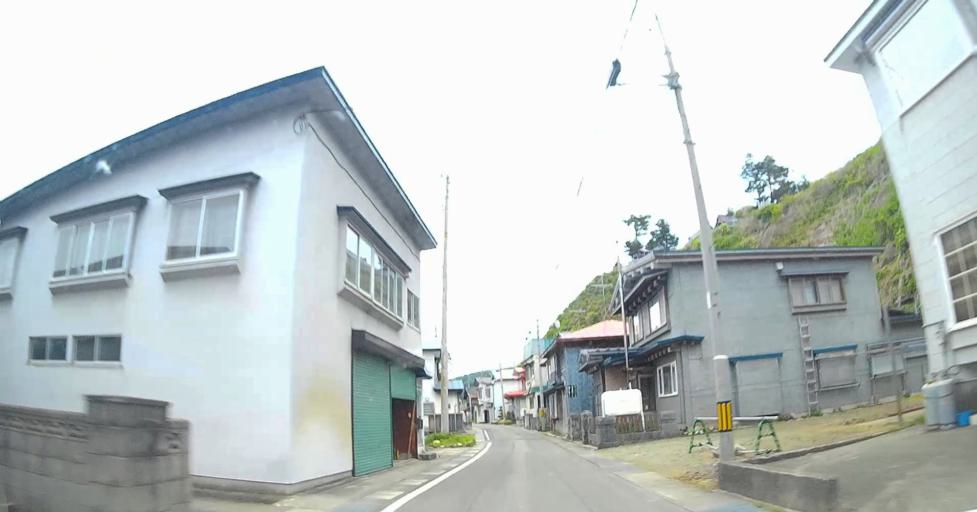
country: JP
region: Aomori
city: Shimokizukuri
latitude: 41.2005
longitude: 140.4298
